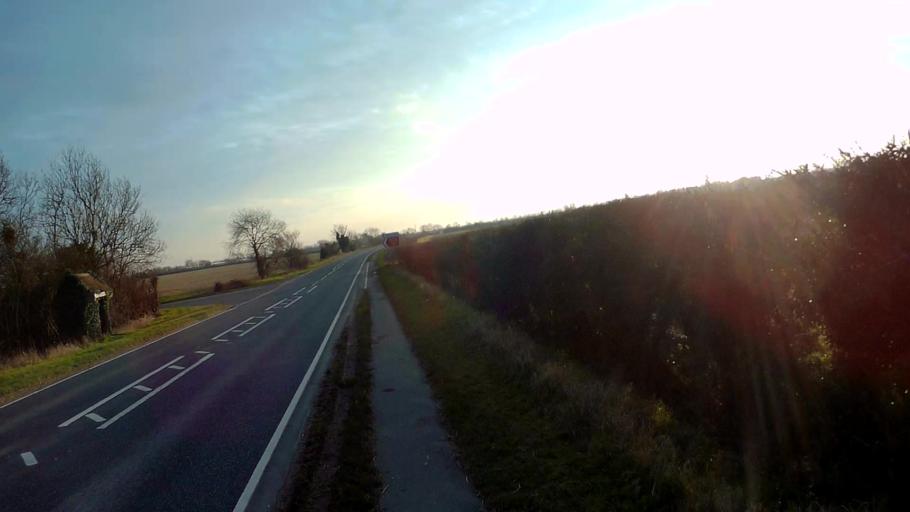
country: GB
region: England
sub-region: Lincolnshire
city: Bourne
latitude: 52.7894
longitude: -0.3764
